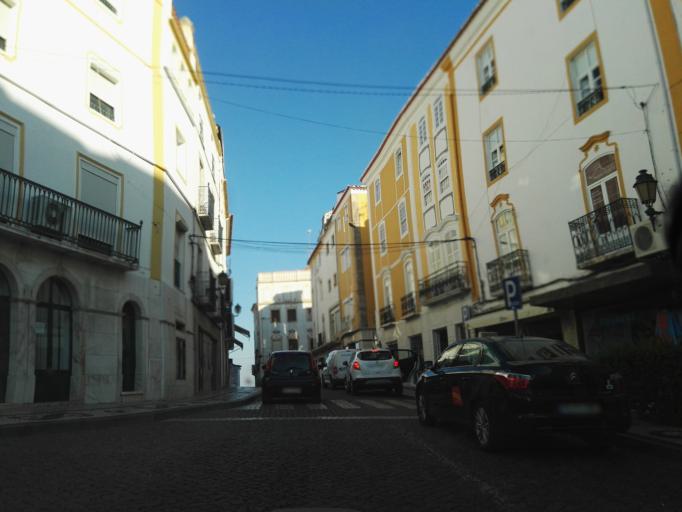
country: PT
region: Portalegre
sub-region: Elvas
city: Elvas
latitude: 38.8800
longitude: -7.1636
